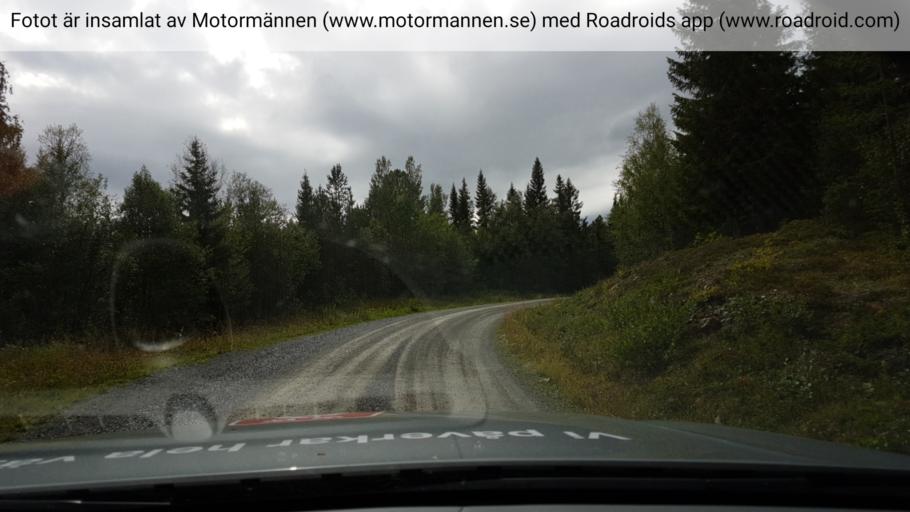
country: SE
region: Jaemtland
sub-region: Krokoms Kommun
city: Valla
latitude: 63.5240
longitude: 13.8979
